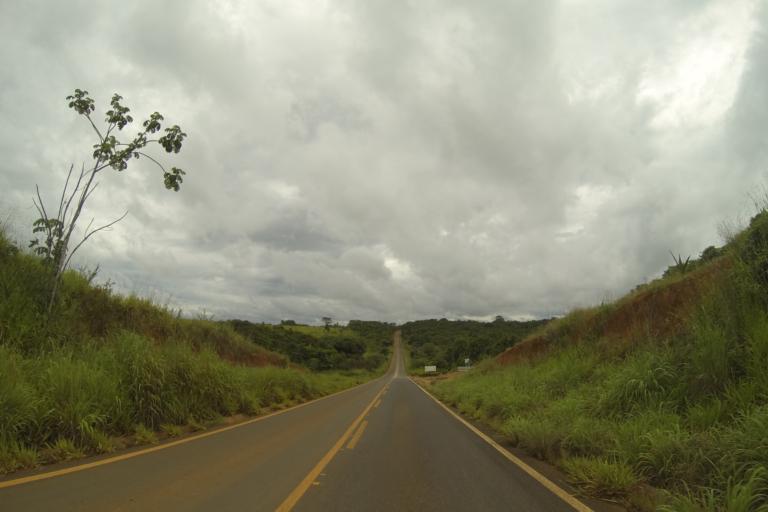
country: BR
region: Minas Gerais
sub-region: Bambui
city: Bambui
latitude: -20.0768
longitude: -46.1514
